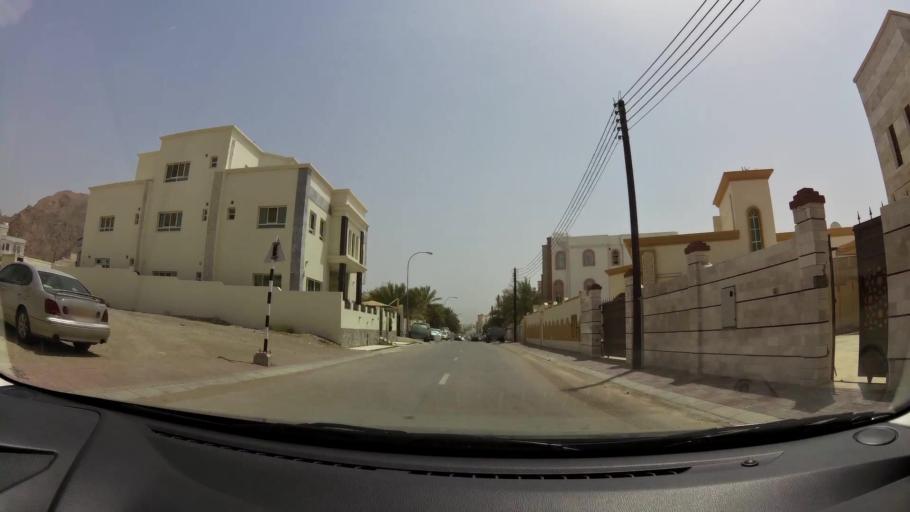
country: OM
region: Muhafazat Masqat
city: Bawshar
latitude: 23.5353
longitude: 58.3849
